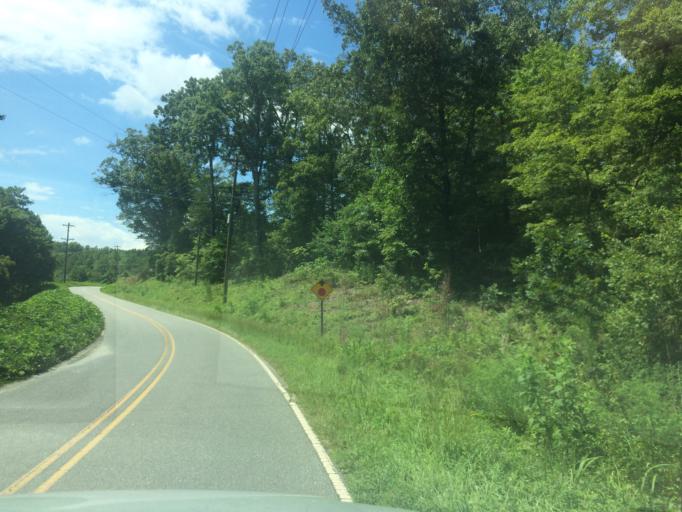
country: US
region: North Carolina
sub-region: Rutherford County
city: Lake Lure
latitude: 35.3916
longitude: -82.1919
